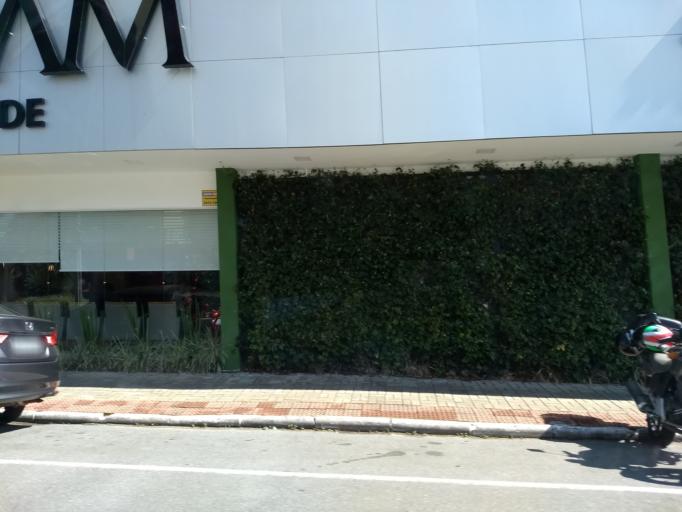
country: BR
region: Santa Catarina
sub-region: Jaragua Do Sul
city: Jaragua do Sul
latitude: -26.4915
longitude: -49.0785
